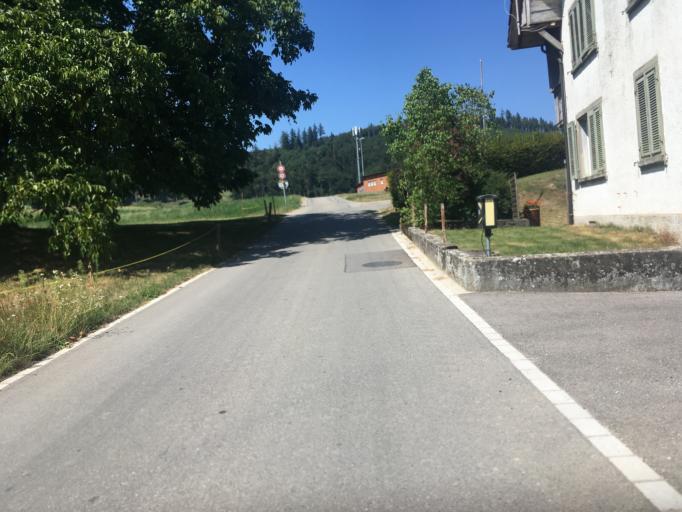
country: CH
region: Bern
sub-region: Biel/Bienne District
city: Meinisberg
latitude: 47.1147
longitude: 7.3571
